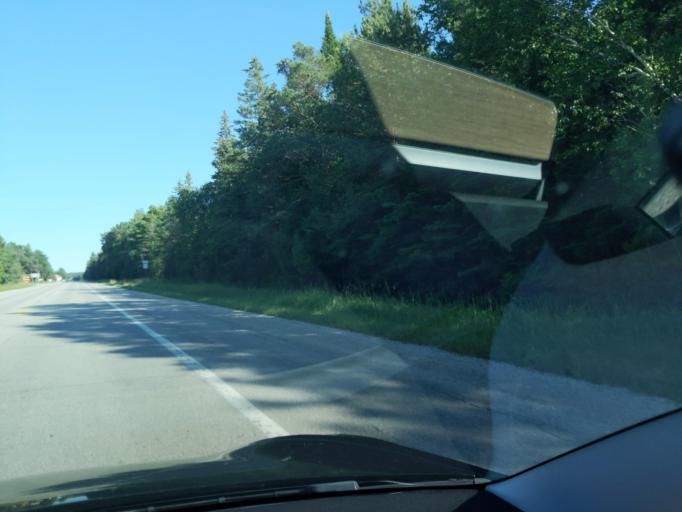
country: US
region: Michigan
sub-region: Mackinac County
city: Saint Ignace
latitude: 45.7589
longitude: -84.7058
